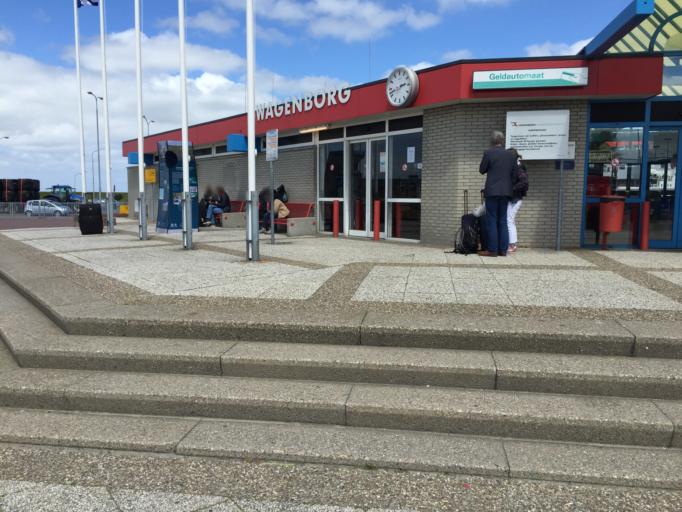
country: NL
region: Friesland
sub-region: Gemeente Dongeradeel
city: Anjum
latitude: 53.4102
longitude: 6.1965
